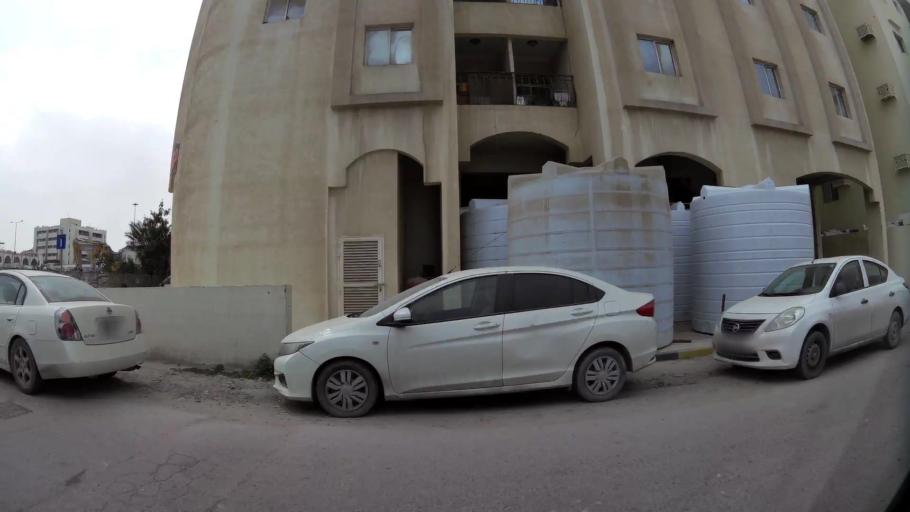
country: QA
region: Baladiyat ad Dawhah
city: Doha
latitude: 25.2837
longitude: 51.5456
